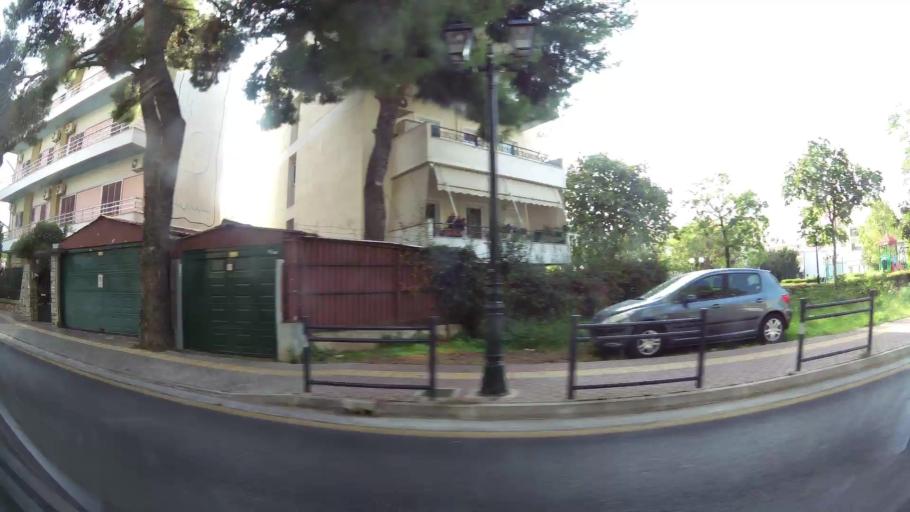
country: GR
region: Attica
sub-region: Nomarchia Athinas
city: Cholargos
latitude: 38.0037
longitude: 23.8129
